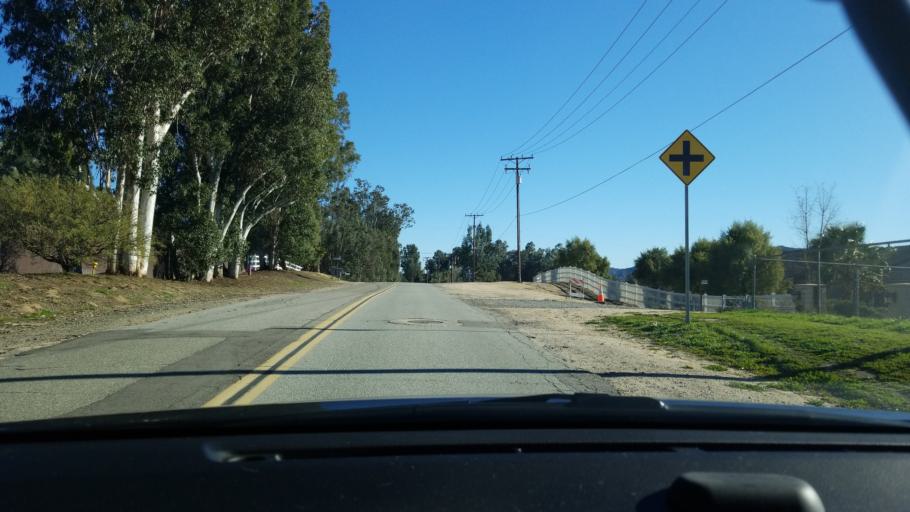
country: US
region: California
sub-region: Riverside County
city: Murrieta
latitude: 33.5463
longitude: -117.2062
